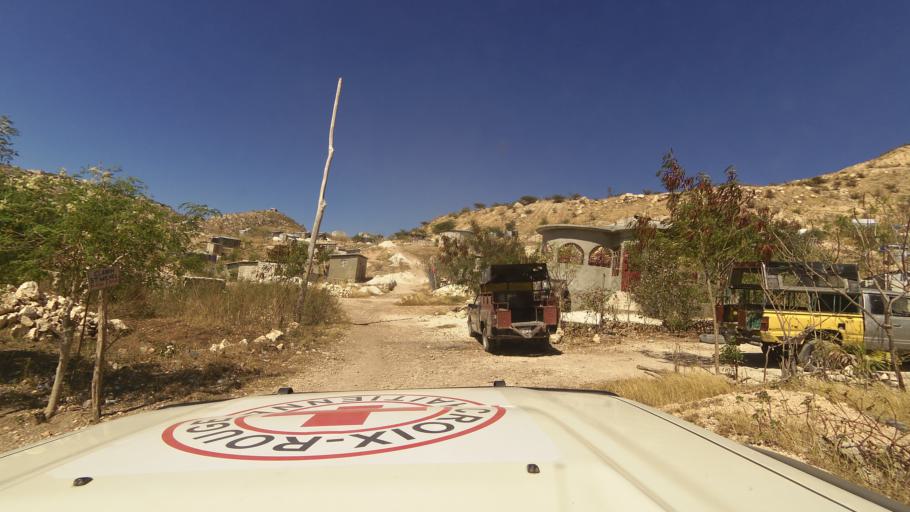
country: HT
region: Ouest
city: Croix des Bouquets
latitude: 18.6648
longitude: -72.2703
